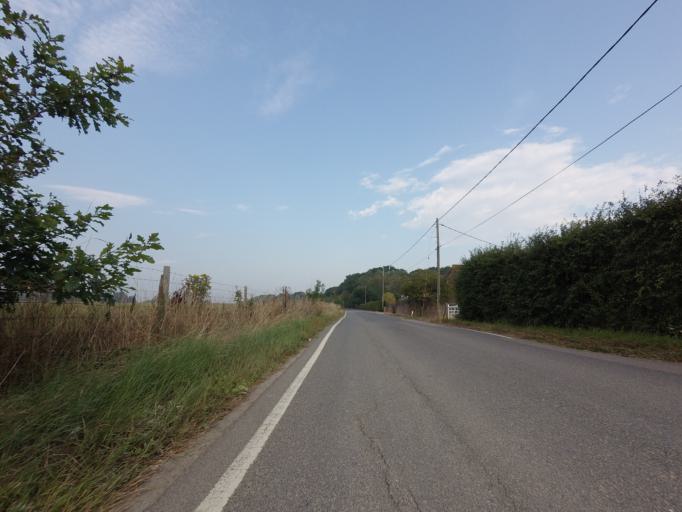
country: GB
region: England
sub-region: Kent
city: Ashford
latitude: 51.1079
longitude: 0.7855
